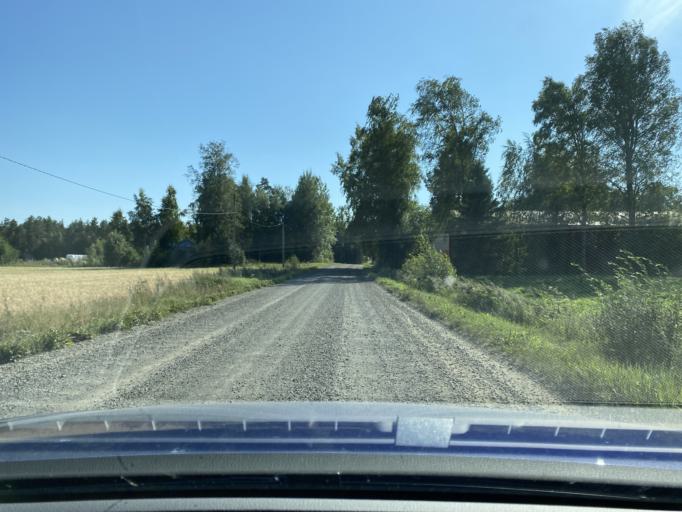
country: FI
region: Satakunta
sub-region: Rauma
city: Kiukainen
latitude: 61.1447
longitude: 21.9984
